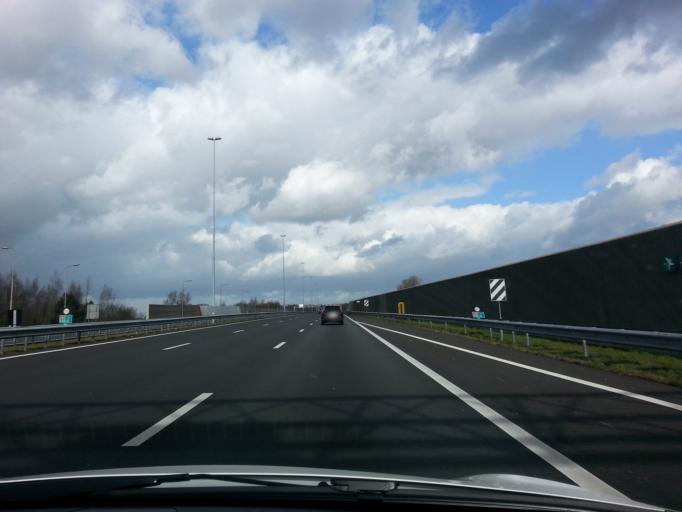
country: NL
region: North Brabant
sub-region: Gemeente Boxtel
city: Boxtel
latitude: 51.5763
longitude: 5.3564
